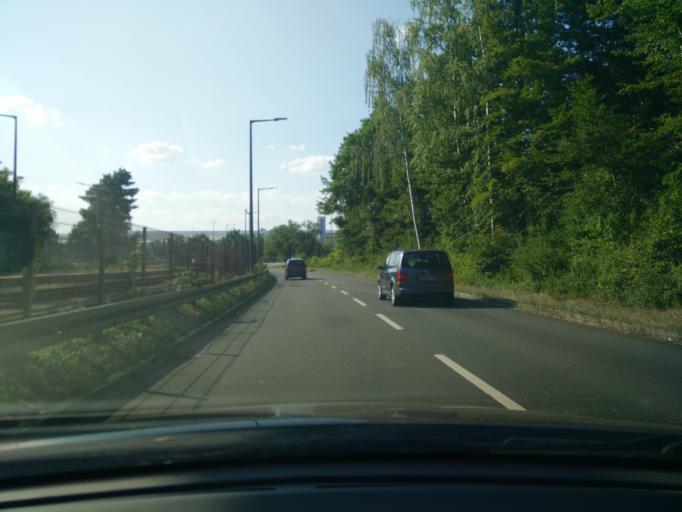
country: DE
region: Bavaria
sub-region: Regierungsbezirk Mittelfranken
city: Nuernberg
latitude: 49.4149
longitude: 11.1187
